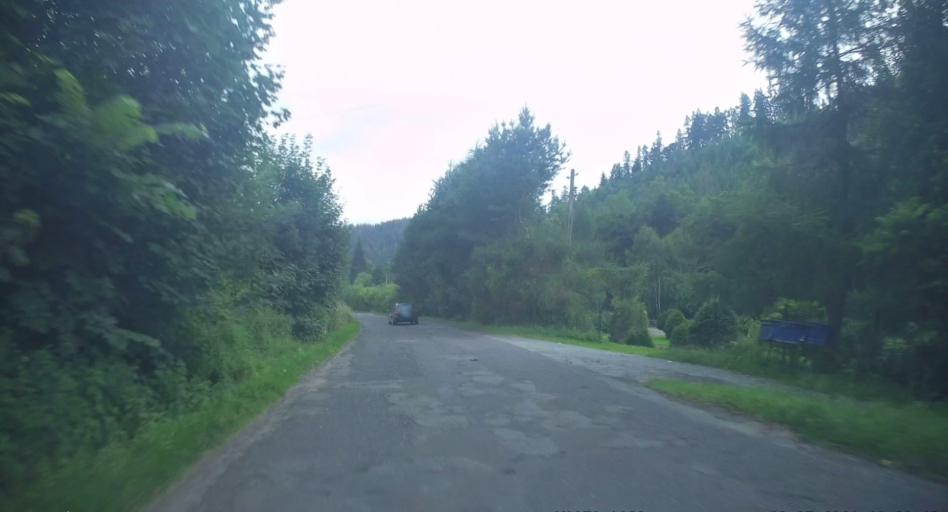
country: PL
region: Lower Silesian Voivodeship
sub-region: Powiat klodzki
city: Ludwikowice Klodzkie
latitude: 50.6291
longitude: 16.4625
